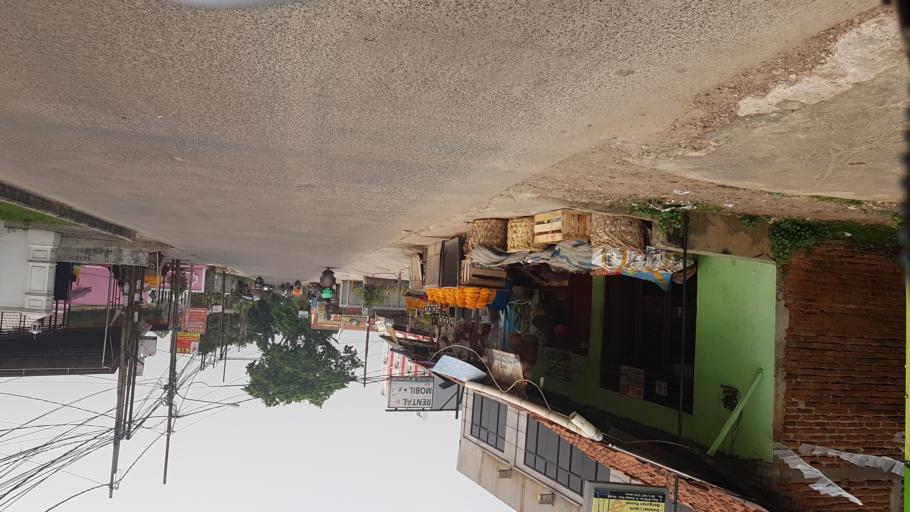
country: ID
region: West Java
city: Depok
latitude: -6.3702
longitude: 106.8426
